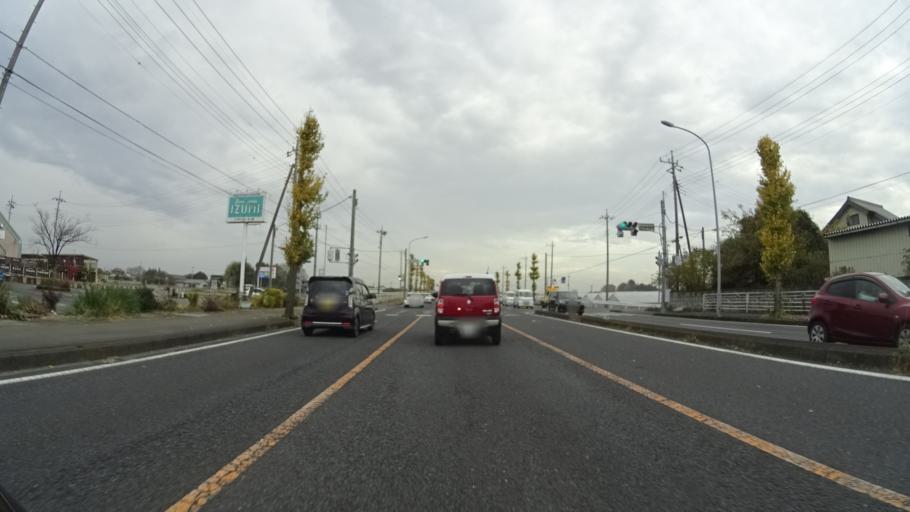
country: JP
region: Gunma
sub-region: Sawa-gun
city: Tamamura
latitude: 36.3701
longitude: 139.1443
